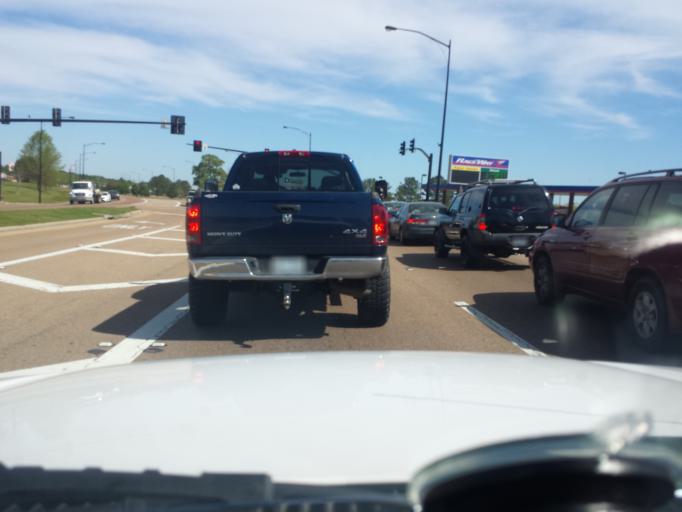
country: US
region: Mississippi
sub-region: Rankin County
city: Pearl
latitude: 32.2753
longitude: -90.0720
